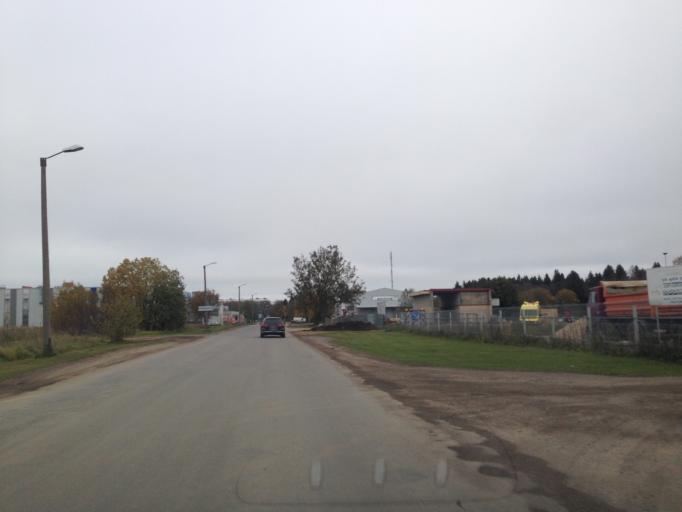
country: EE
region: Harju
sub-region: Harku vald
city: Tabasalu
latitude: 59.4227
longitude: 24.5402
